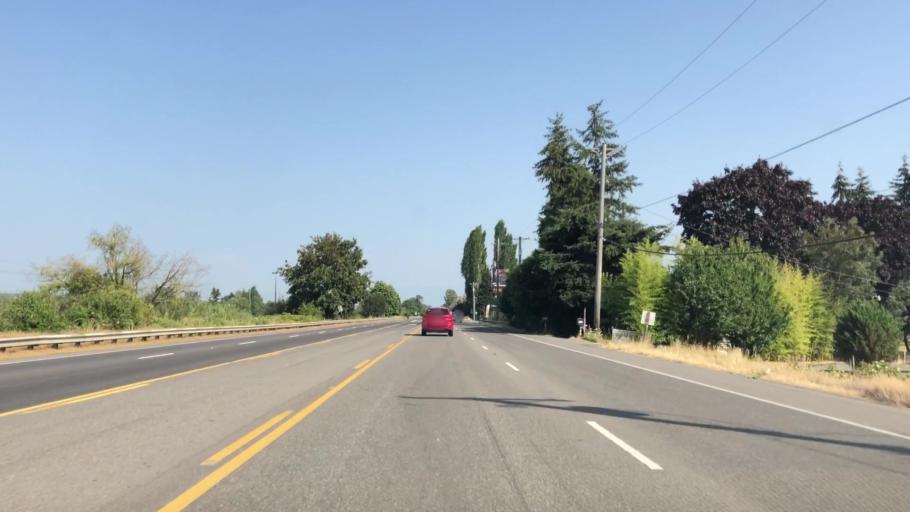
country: US
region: Washington
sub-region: Pierce County
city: Fife
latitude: 47.2303
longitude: -122.3786
